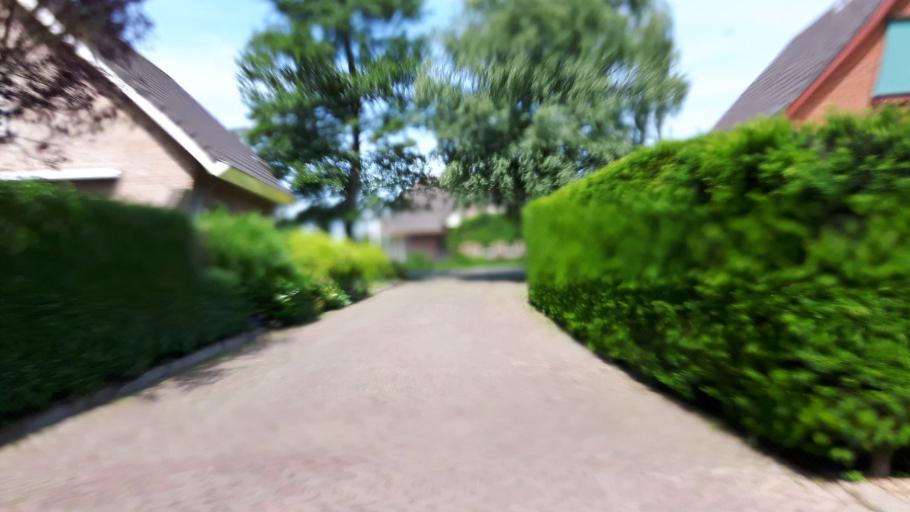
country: NL
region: Utrecht
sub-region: Gemeente Woerden
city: Woerden
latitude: 52.0931
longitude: 4.8767
